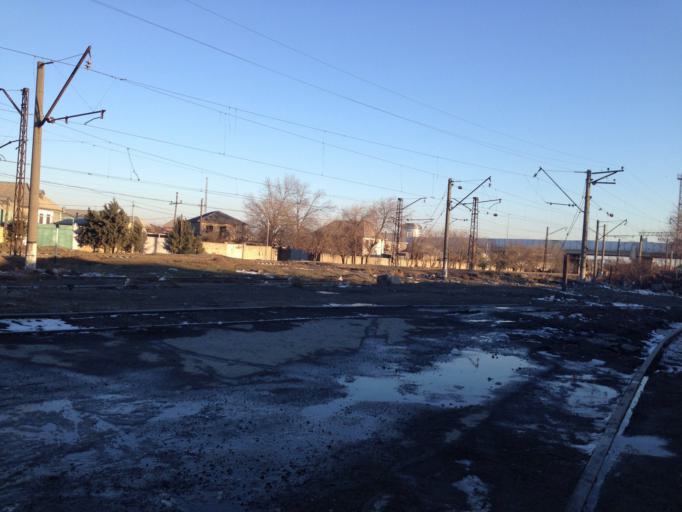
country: AZ
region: Baki
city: Baku
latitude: 40.4218
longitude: 49.8662
